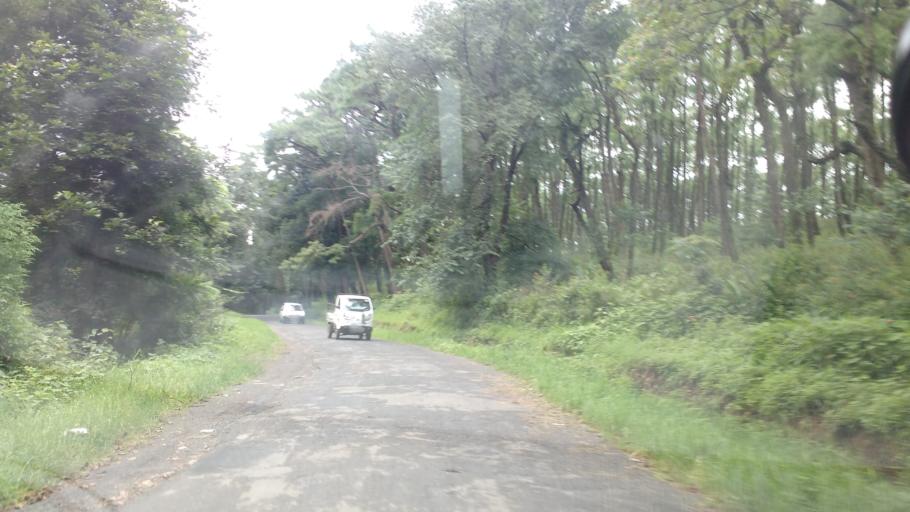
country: IN
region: Meghalaya
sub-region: East Khasi Hills
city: Shillong
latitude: 25.5456
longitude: 91.8339
